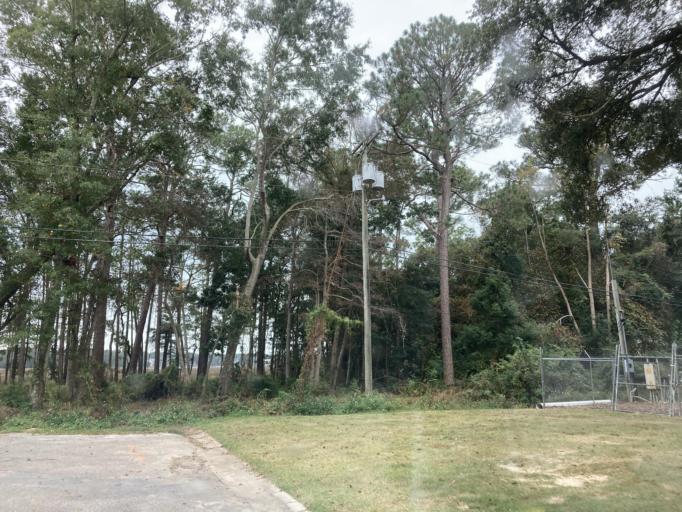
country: US
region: Mississippi
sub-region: Jackson County
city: Ocean Springs
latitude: 30.4286
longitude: -88.8228
